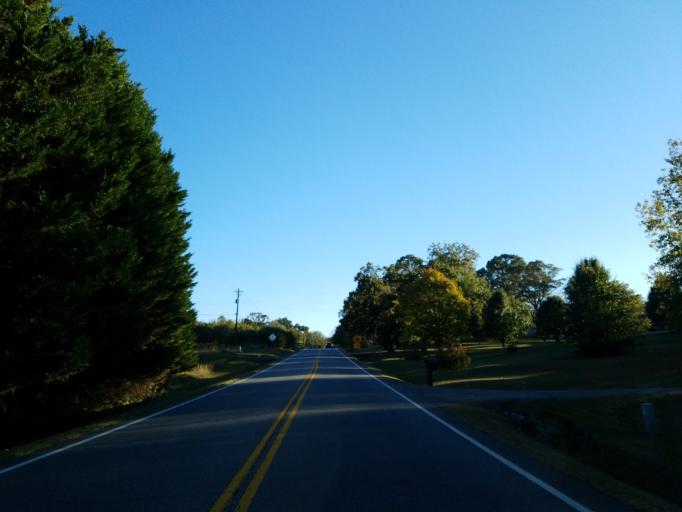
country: US
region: Georgia
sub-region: Dawson County
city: Dawsonville
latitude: 34.4110
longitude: -84.1166
